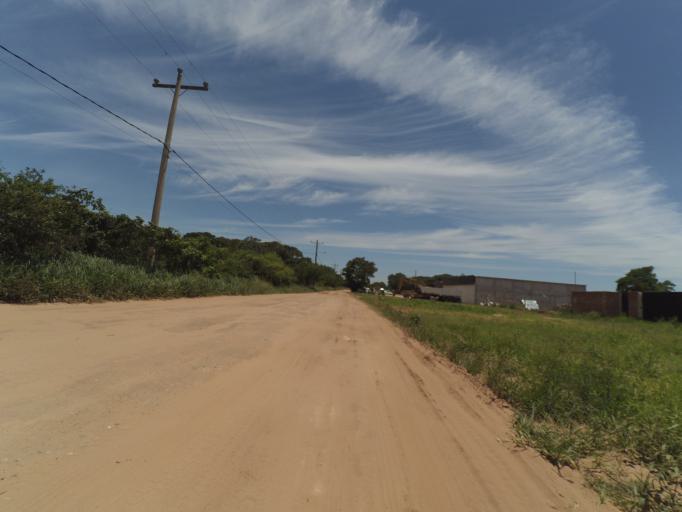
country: BO
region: Santa Cruz
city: Santa Cruz de la Sierra
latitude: -17.8122
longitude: -63.2346
